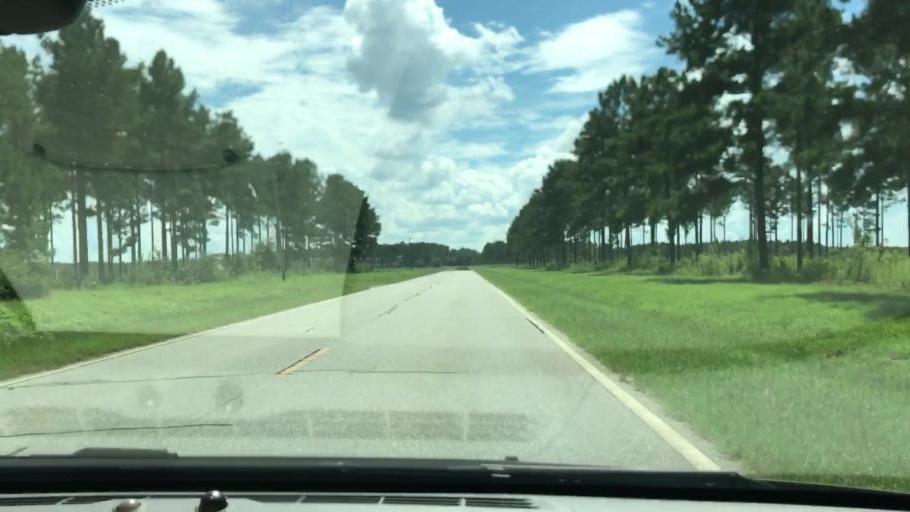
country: US
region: Georgia
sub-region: Quitman County
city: Georgetown
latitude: 32.0586
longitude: -85.0363
